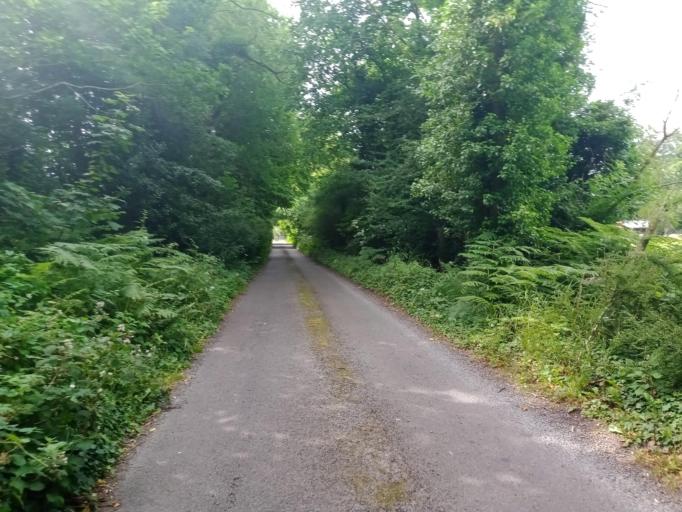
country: IE
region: Leinster
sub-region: Laois
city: Abbeyleix
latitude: 52.8984
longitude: -7.3607
